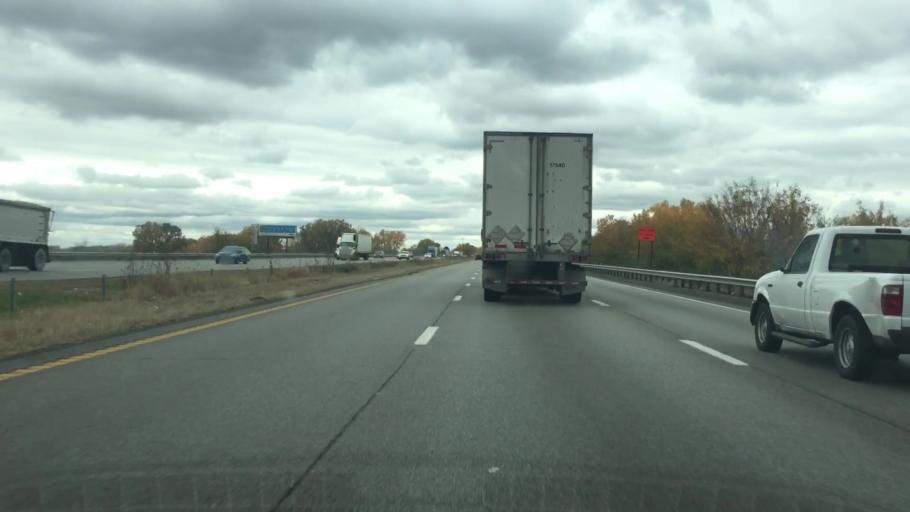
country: US
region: Missouri
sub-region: Jackson County
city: Sugar Creek
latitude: 39.1223
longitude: -94.4931
